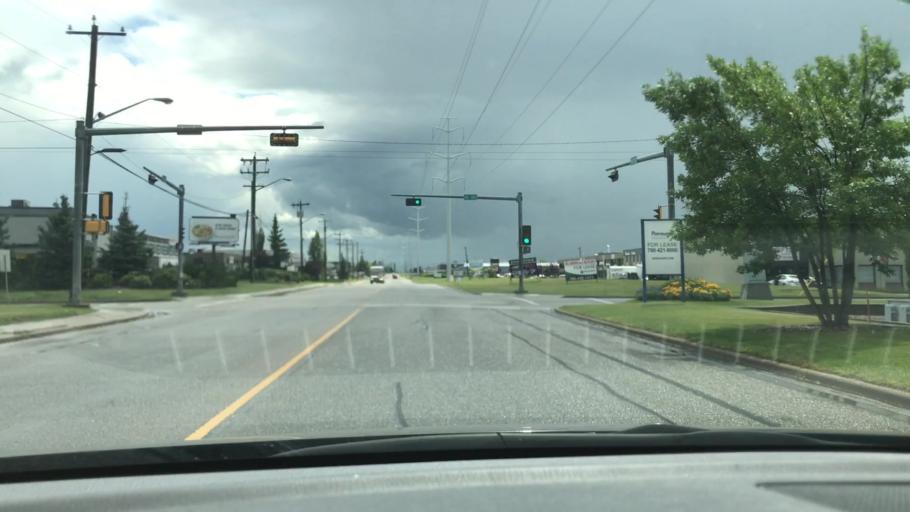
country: CA
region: Alberta
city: Edmonton
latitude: 53.4794
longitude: -113.4792
